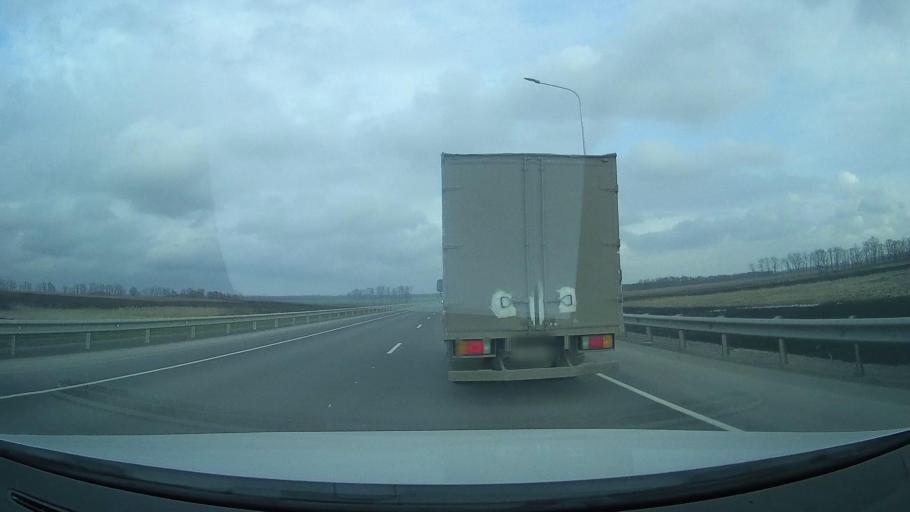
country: RU
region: Rostov
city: Grushevskaya
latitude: 47.4623
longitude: 39.8902
